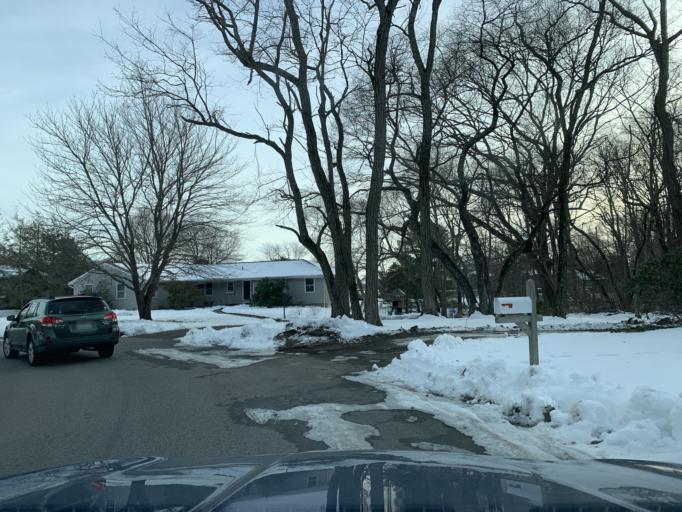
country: US
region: Rhode Island
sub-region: Washington County
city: North Kingstown
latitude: 41.5888
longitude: -71.4408
